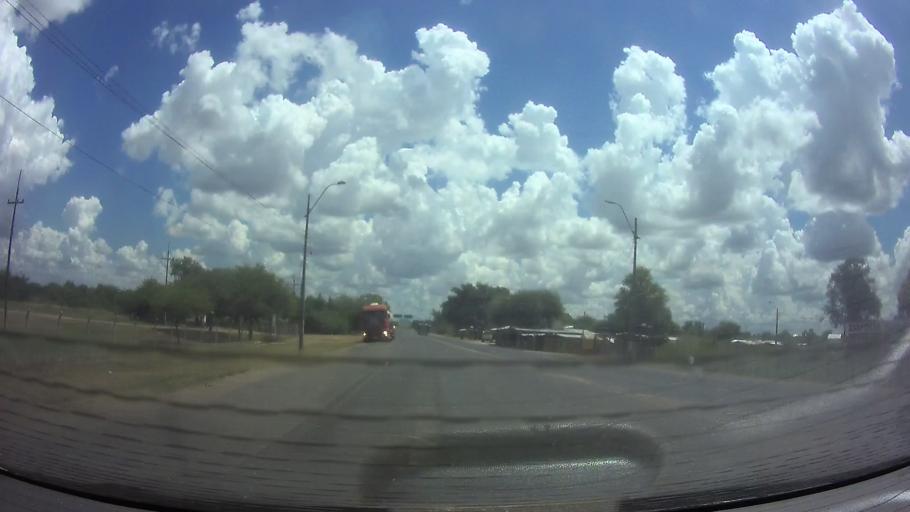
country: PY
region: Central
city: Colonia Mariano Roque Alonso
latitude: -25.1719
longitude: -57.5673
